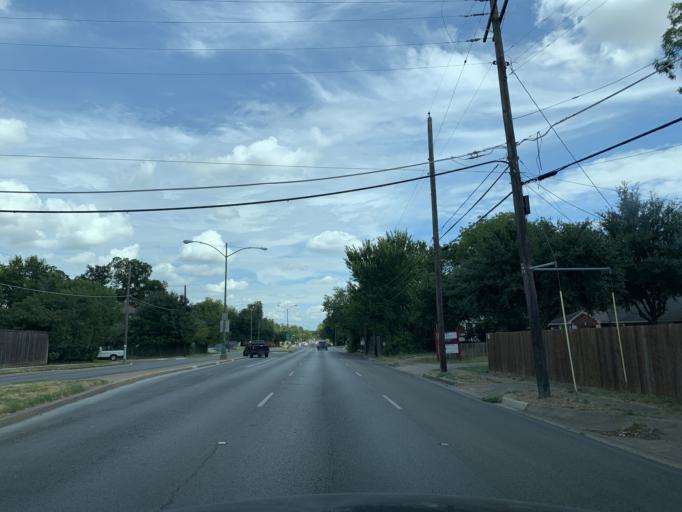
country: US
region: Texas
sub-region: Dallas County
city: Cockrell Hill
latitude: 32.7460
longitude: -96.8498
